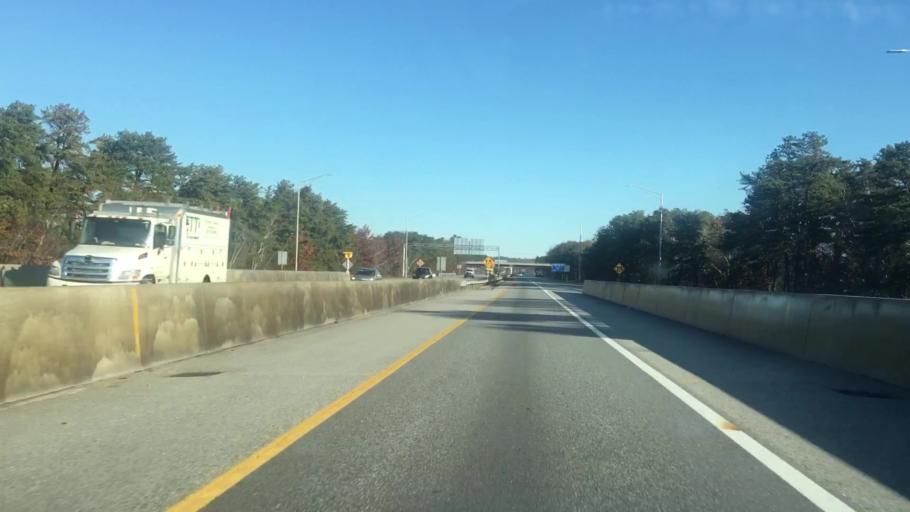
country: US
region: Maine
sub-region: Cumberland County
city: New Gloucester
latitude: 43.9370
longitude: -70.3347
